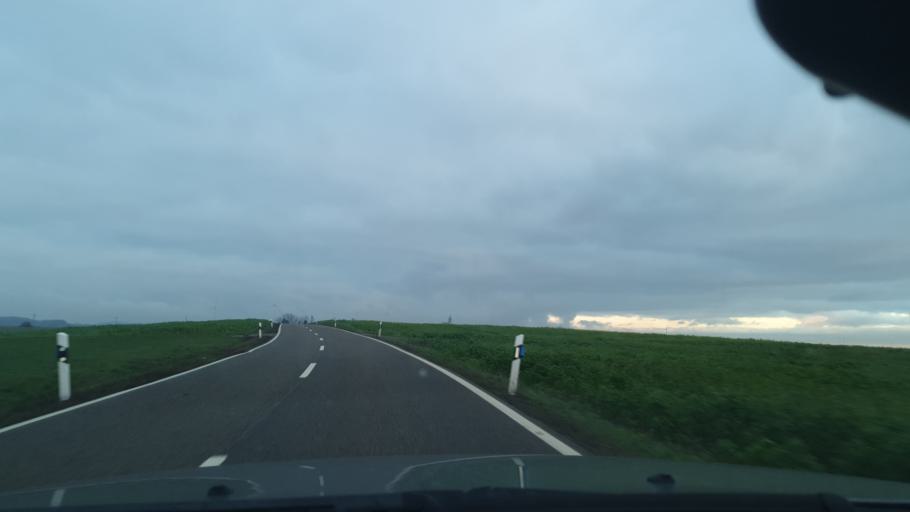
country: DE
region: Rheinland-Pfalz
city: Martinshohe
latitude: 49.3635
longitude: 7.4600
